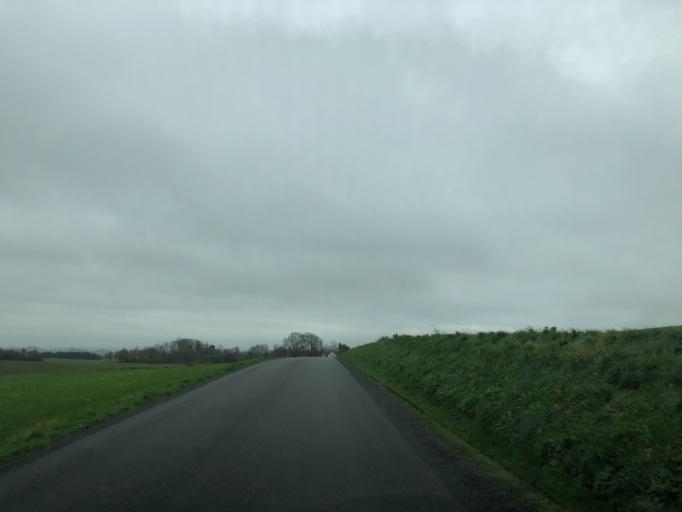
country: DK
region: Central Jutland
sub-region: Skanderborg Kommune
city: Ry
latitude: 56.0752
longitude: 9.8363
